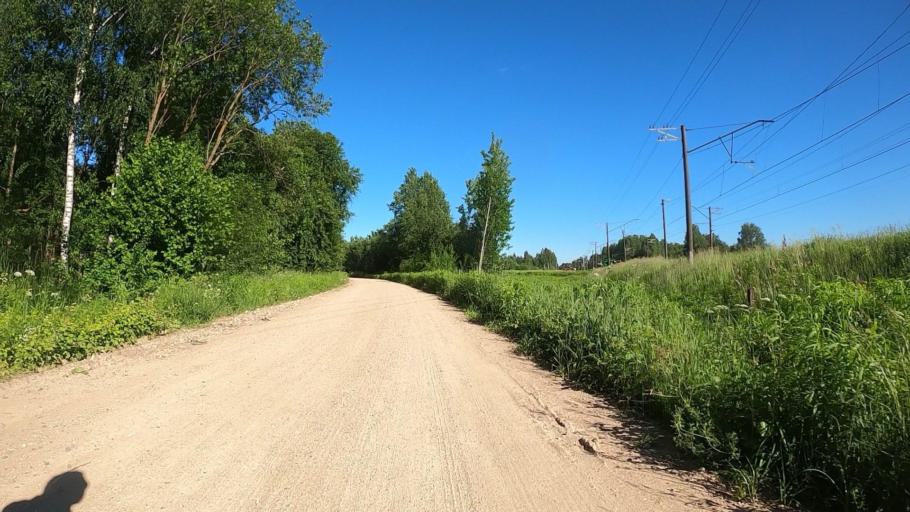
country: LV
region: Ogre
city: Ogre
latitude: 56.7814
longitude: 24.6552
